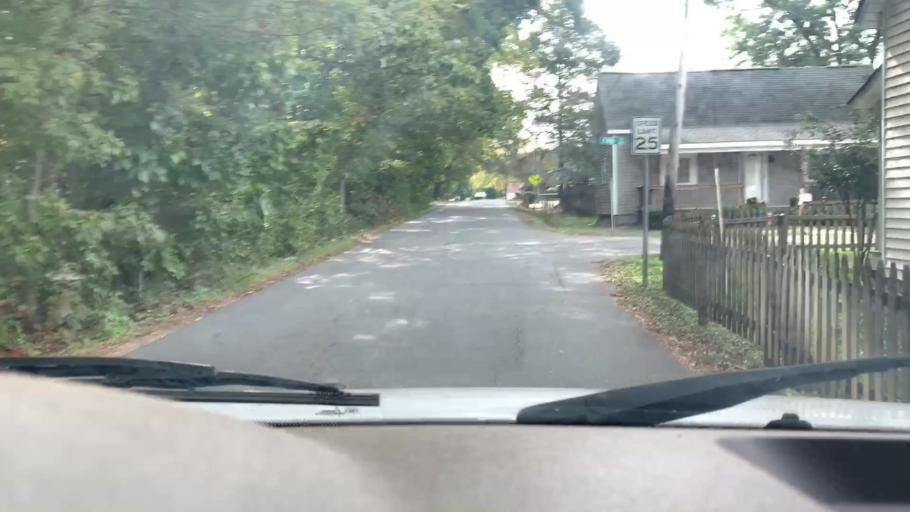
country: US
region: North Carolina
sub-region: Mecklenburg County
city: Huntersville
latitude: 35.4204
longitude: -80.8379
